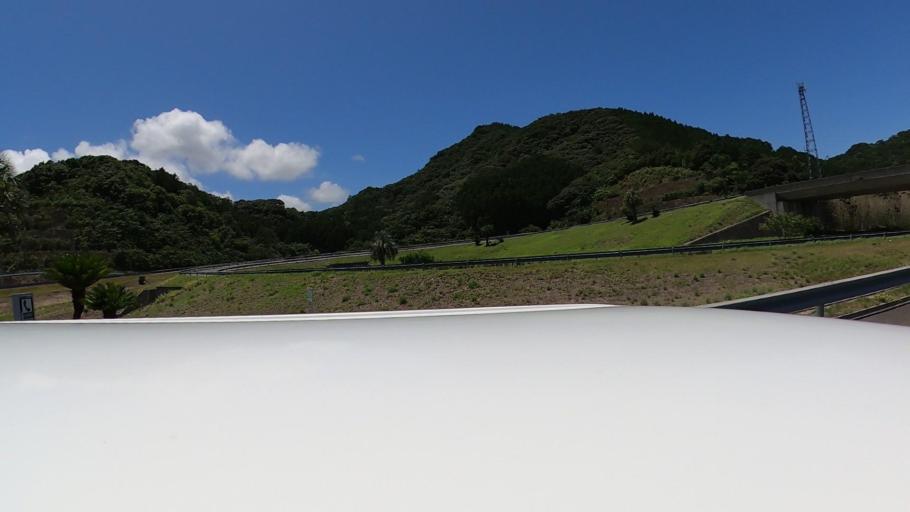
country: JP
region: Miyazaki
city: Nobeoka
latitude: 32.5283
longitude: 131.6653
